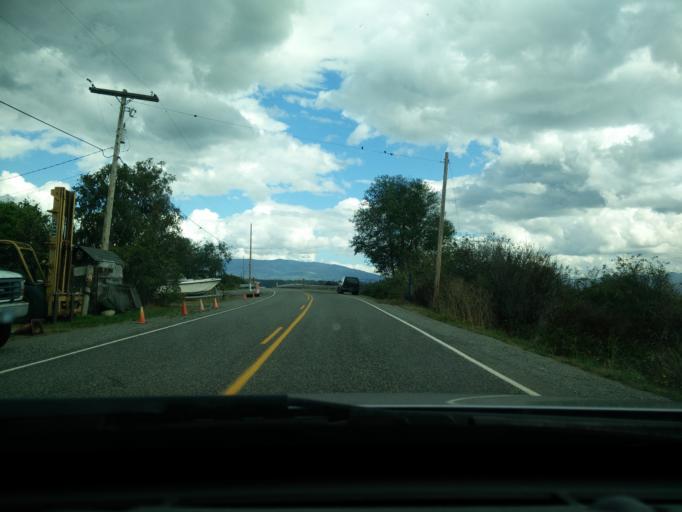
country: US
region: Washington
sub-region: Skagit County
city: Burlington
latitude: 48.5541
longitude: -122.4562
